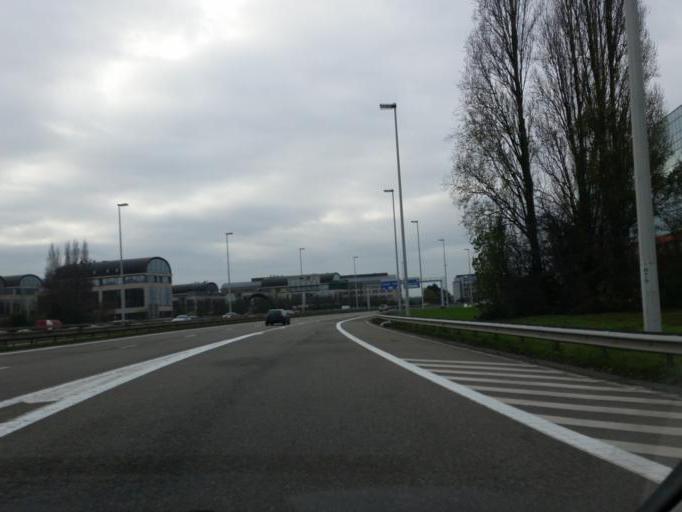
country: BE
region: Flanders
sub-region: Provincie Vlaams-Brabant
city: Diegem
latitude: 50.8877
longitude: 4.4517
